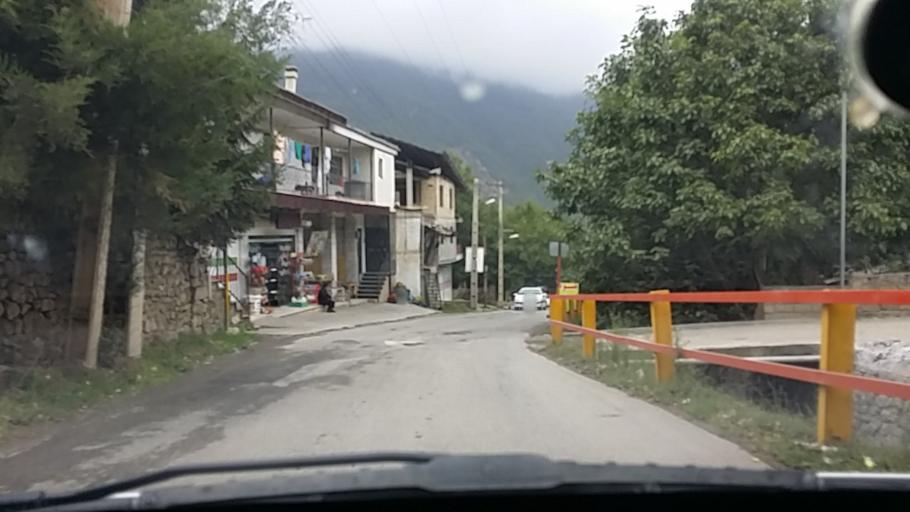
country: IR
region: Mazandaran
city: `Abbasabad
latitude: 36.4831
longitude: 51.1363
